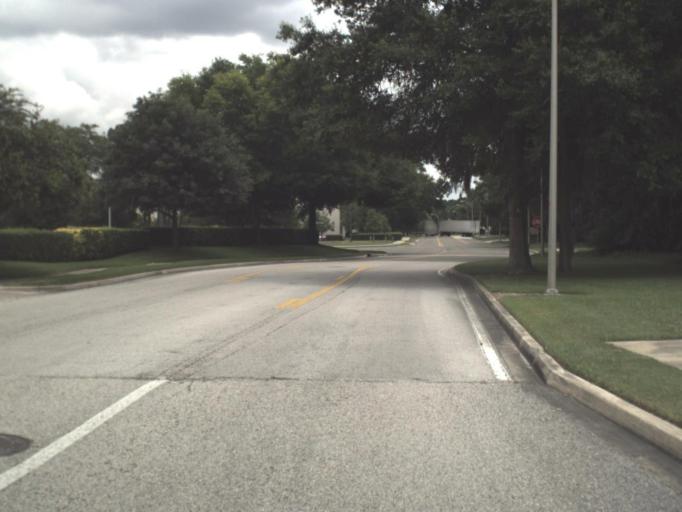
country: US
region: Florida
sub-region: Duval County
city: Jacksonville
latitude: 30.4740
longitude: -81.6634
